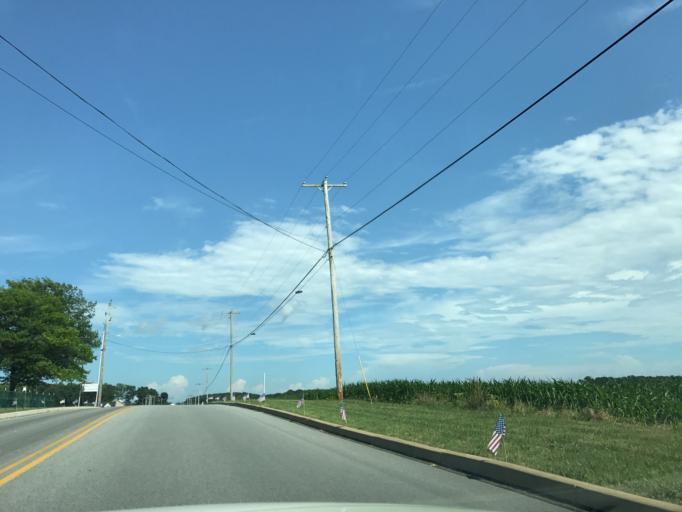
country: US
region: Pennsylvania
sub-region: York County
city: Parkville
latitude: 39.7690
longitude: -76.9817
